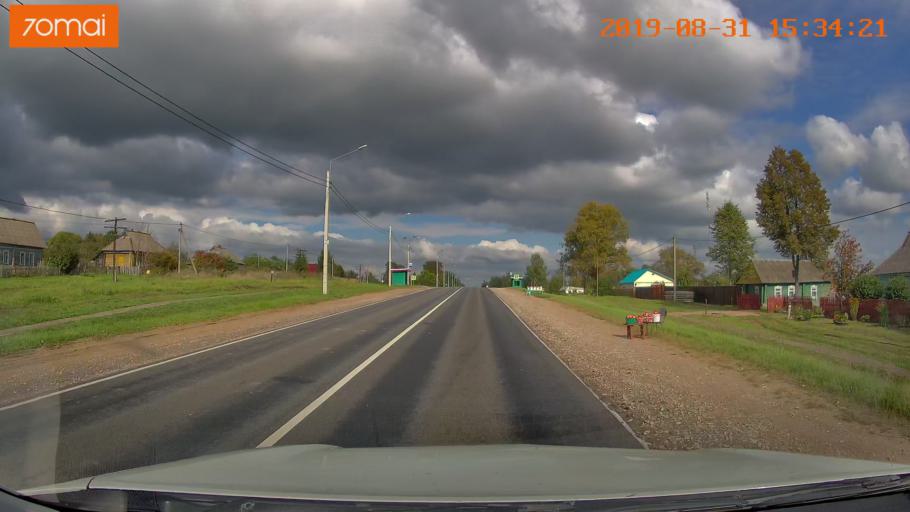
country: RU
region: Kaluga
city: Mosal'sk
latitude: 54.6001
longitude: 34.7186
